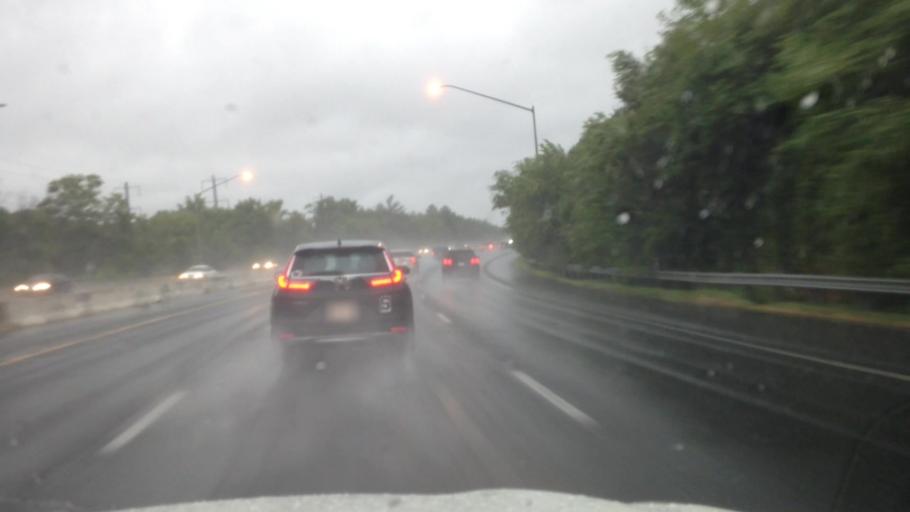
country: US
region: Maryland
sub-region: Prince George's County
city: Landover Hills
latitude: 38.9392
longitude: -76.8849
